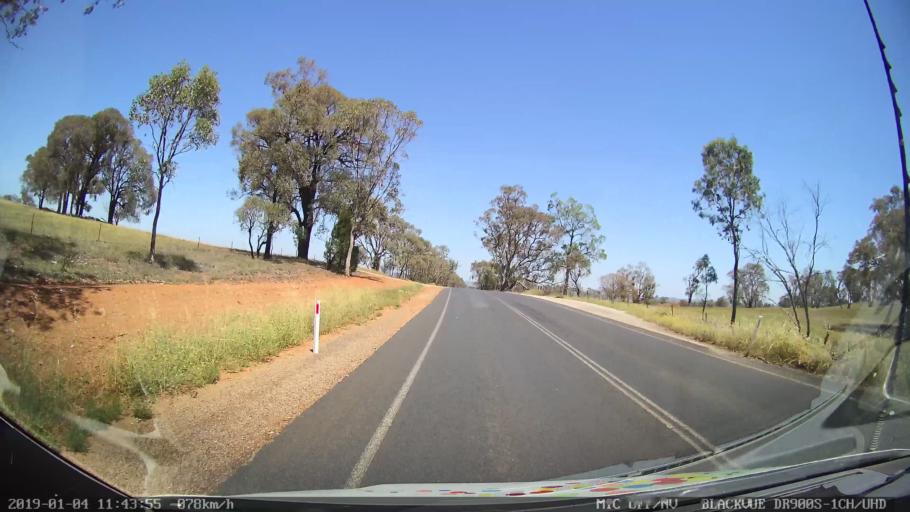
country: AU
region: New South Wales
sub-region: Cabonne
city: Molong
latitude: -32.9653
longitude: 148.7796
